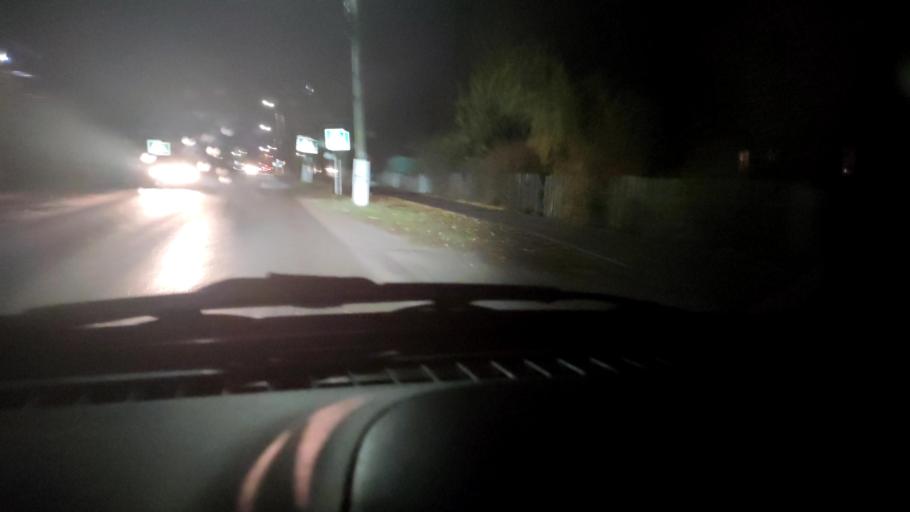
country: RU
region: Voronezj
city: Latnaya
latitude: 51.6560
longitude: 38.9021
